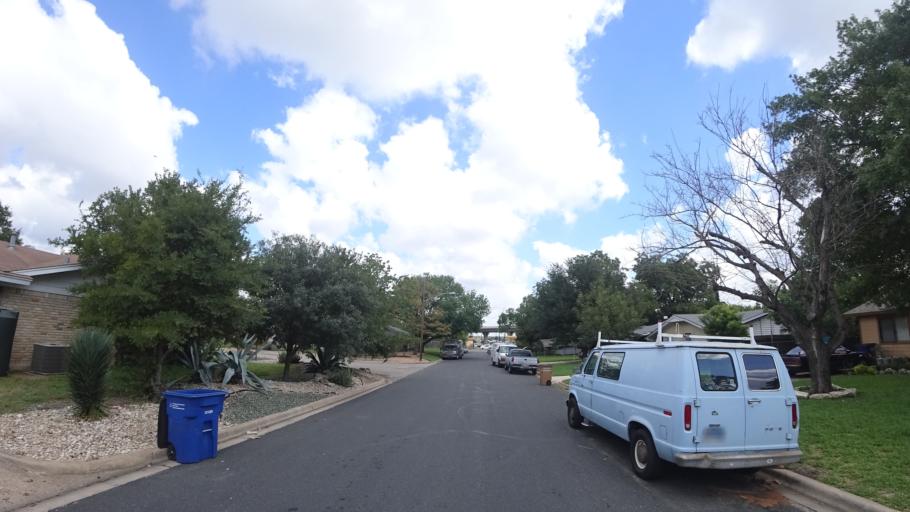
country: US
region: Texas
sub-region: Travis County
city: Wells Branch
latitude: 30.3593
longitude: -97.7182
